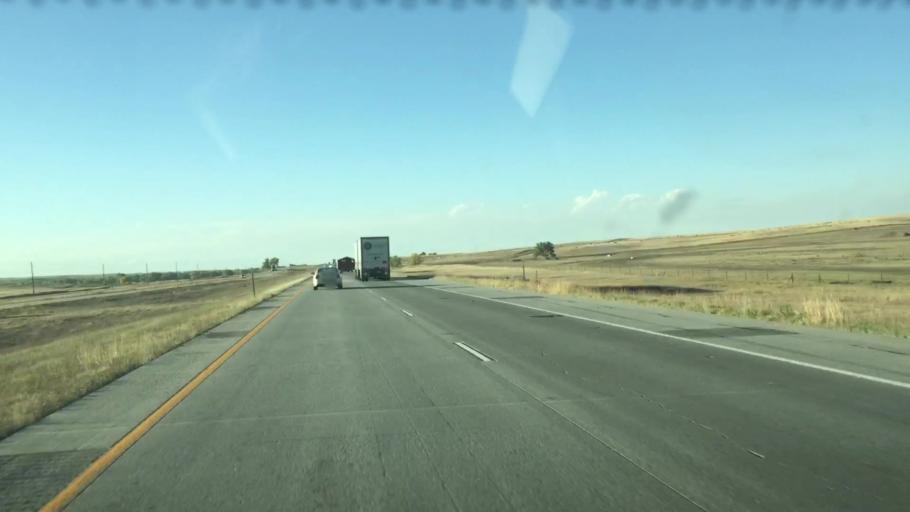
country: US
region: Colorado
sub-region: Arapahoe County
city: Byers
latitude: 39.5427
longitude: -103.9980
